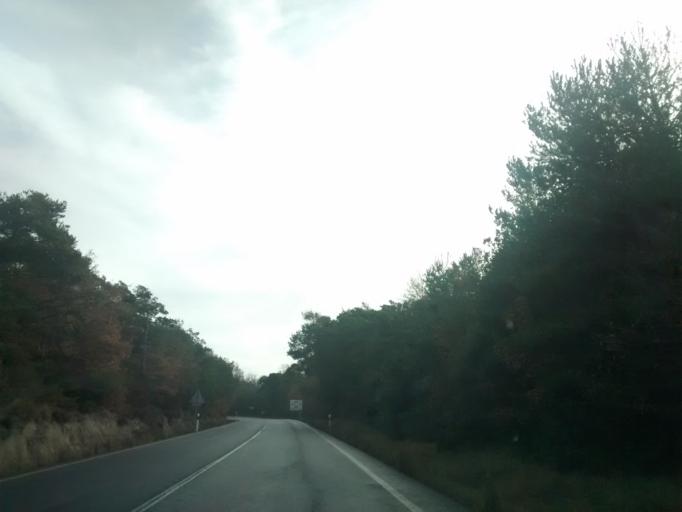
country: ES
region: Aragon
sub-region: Provincia de Zaragoza
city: Mianos
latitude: 42.6093
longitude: -0.9013
